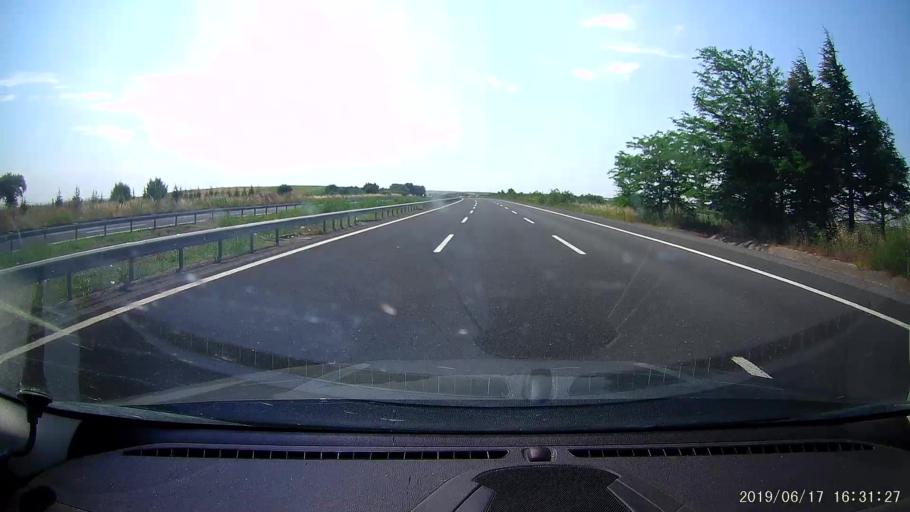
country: TR
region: Tekirdag
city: Beyazkoy
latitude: 41.3620
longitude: 27.6273
